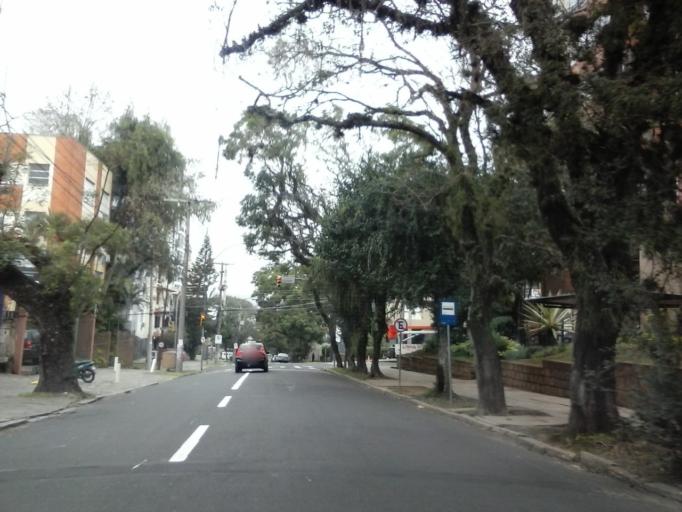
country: BR
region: Rio Grande do Sul
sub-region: Porto Alegre
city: Porto Alegre
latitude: -30.0463
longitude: -51.1856
